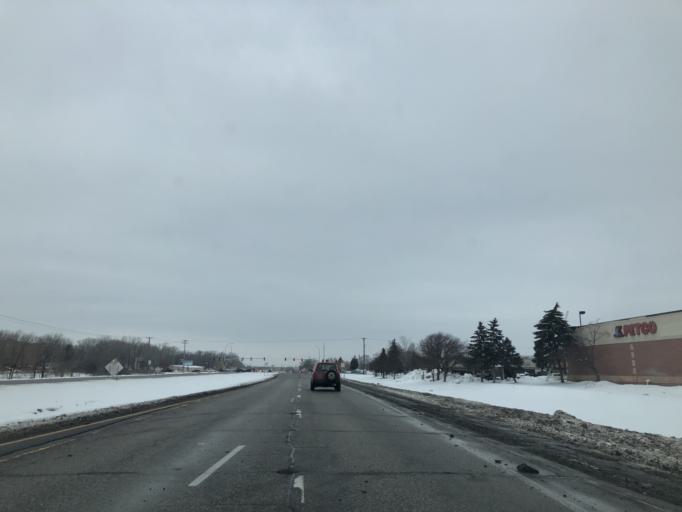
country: US
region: Minnesota
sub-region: Hennepin County
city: Brooklyn Park
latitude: 45.0925
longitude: -93.3827
